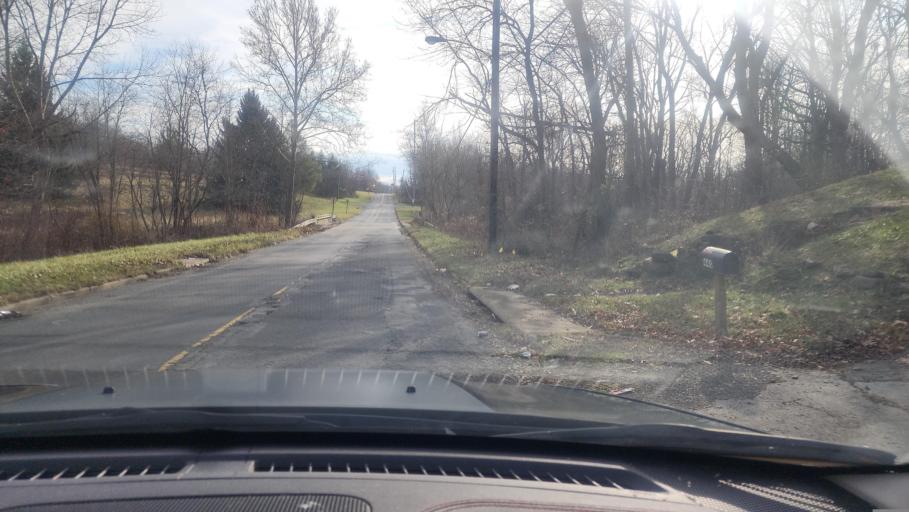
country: US
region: Ohio
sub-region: Mahoning County
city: Campbell
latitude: 41.1034
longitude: -80.6162
